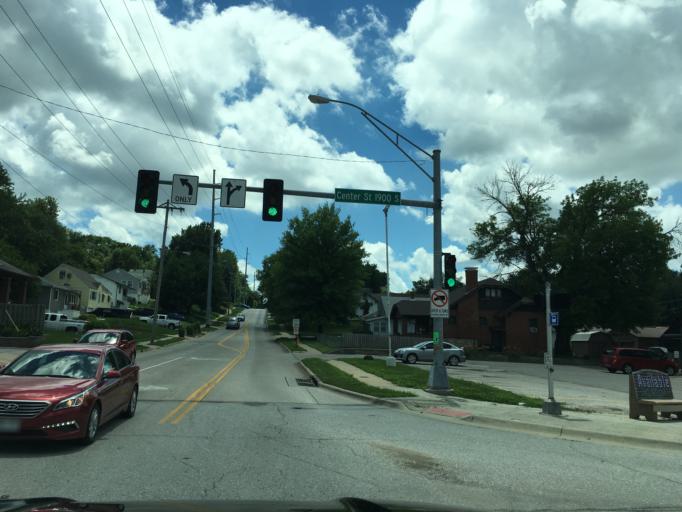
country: US
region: Nebraska
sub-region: Douglas County
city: Omaha
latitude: 41.2416
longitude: -95.9903
